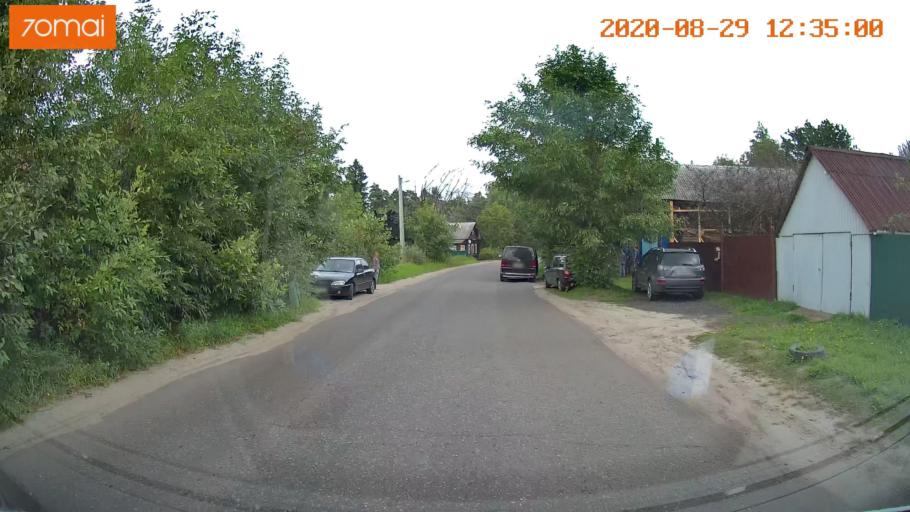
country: RU
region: Ivanovo
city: Yur'yevets
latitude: 57.3120
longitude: 43.1039
